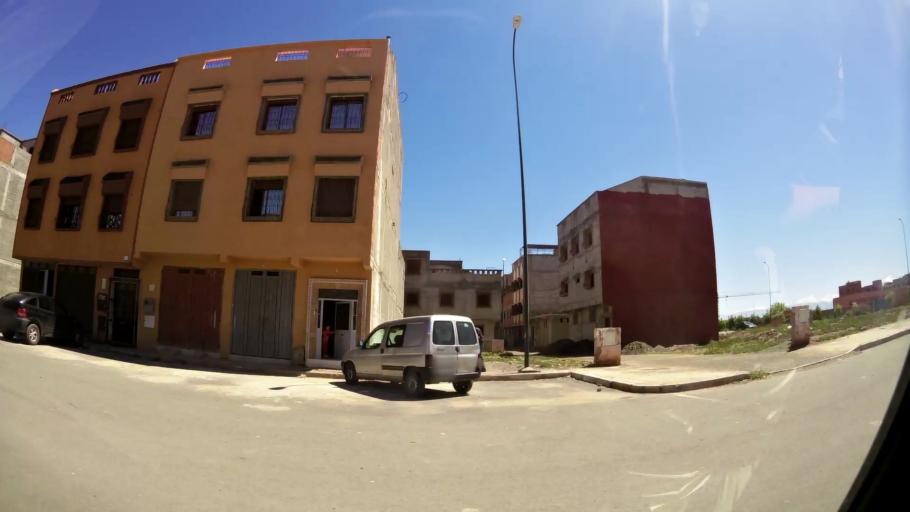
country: MA
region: Marrakech-Tensift-Al Haouz
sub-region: Marrakech
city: Marrakesh
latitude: 31.5530
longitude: -7.9788
